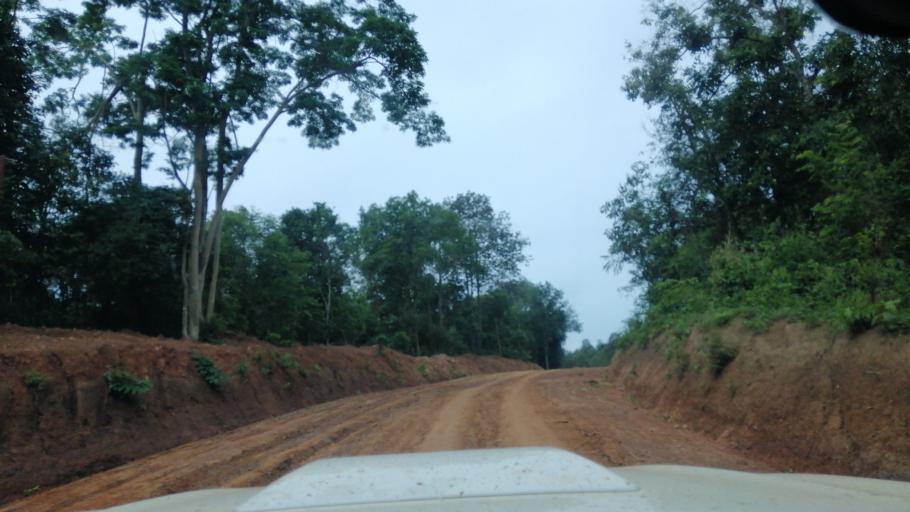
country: TH
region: Loei
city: Na Haeo
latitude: 17.5801
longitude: 101.1723
